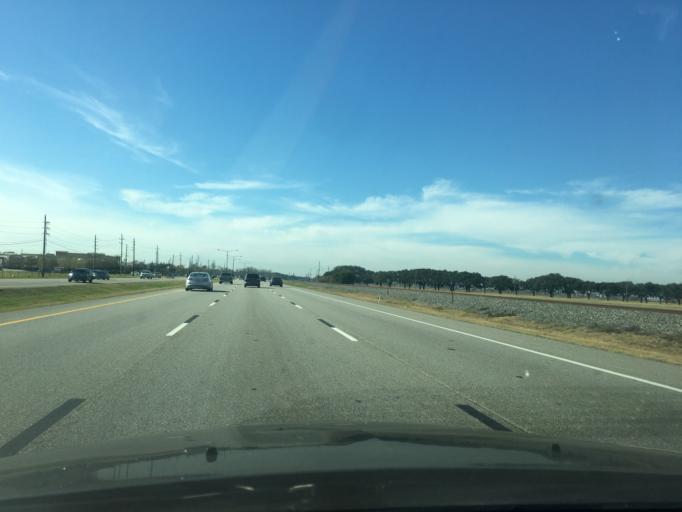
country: US
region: Texas
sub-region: Fort Bend County
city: Sugar Land
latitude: 29.6106
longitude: -95.6556
